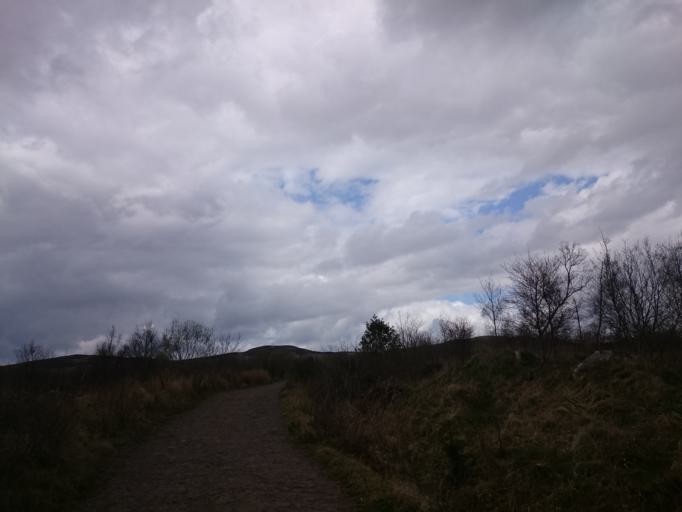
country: GB
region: Scotland
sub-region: Stirling
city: Killearn
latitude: 56.0935
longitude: -4.4882
